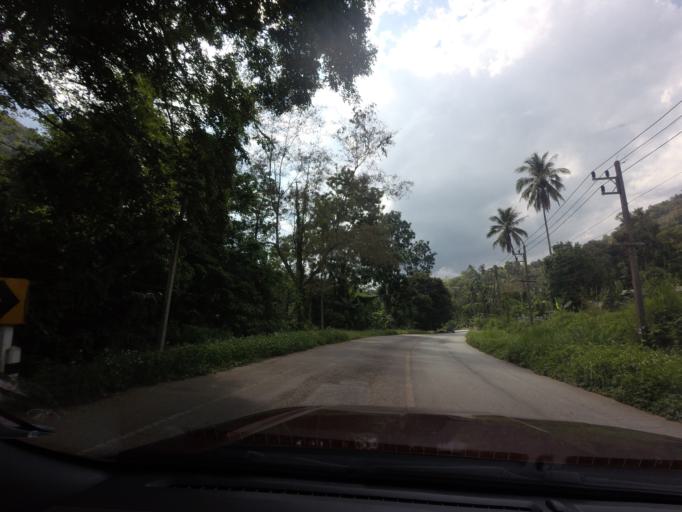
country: TH
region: Yala
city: Than To
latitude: 6.1761
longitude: 101.1759
